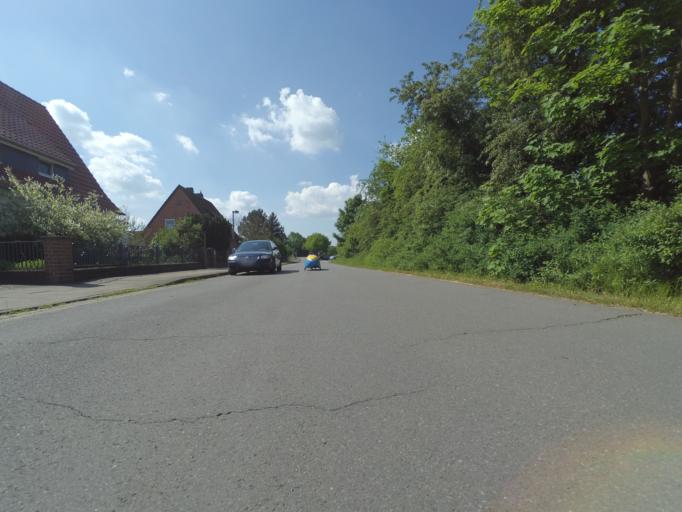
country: DE
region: Lower Saxony
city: Burgdorf
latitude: 52.4893
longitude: 10.0180
